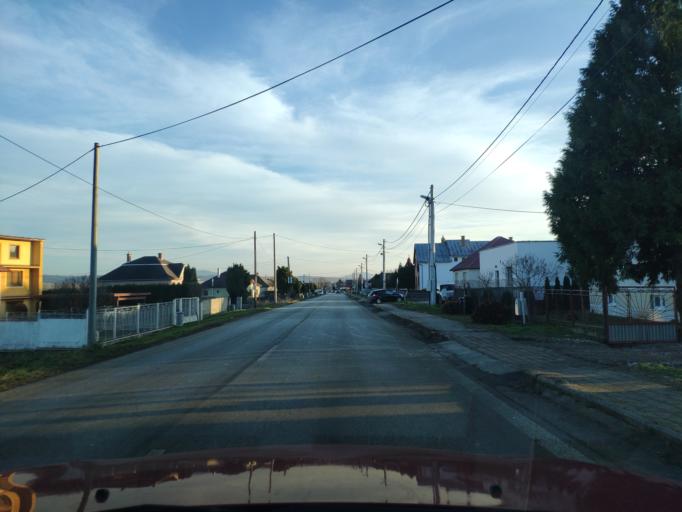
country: SK
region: Kosicky
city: Kosice
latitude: 48.8385
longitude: 21.2833
